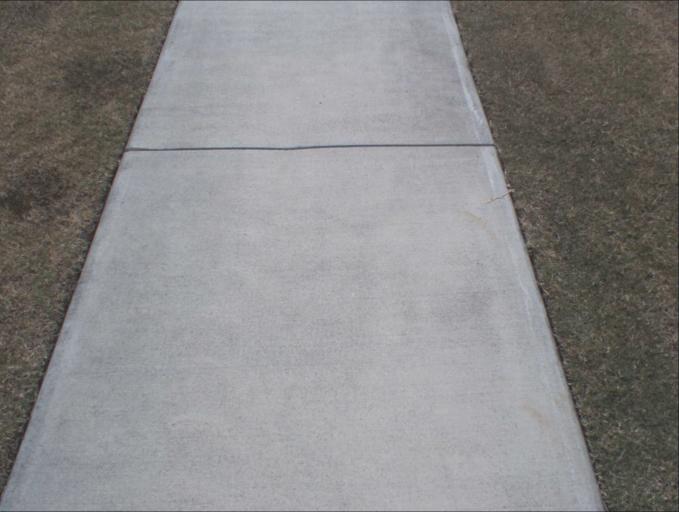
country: AU
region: Queensland
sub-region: Logan
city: Beenleigh
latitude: -27.6628
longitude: 153.2045
